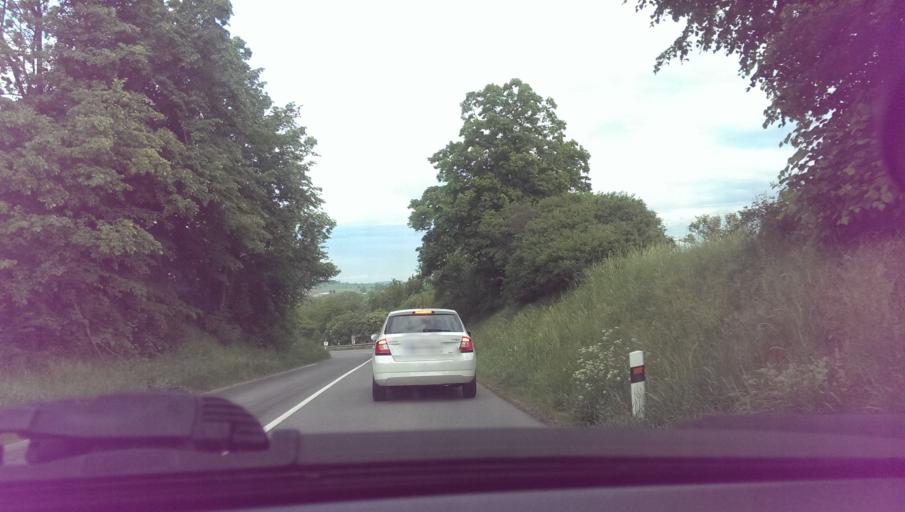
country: CZ
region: Zlin
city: Kvasice
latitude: 49.2481
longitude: 17.4608
